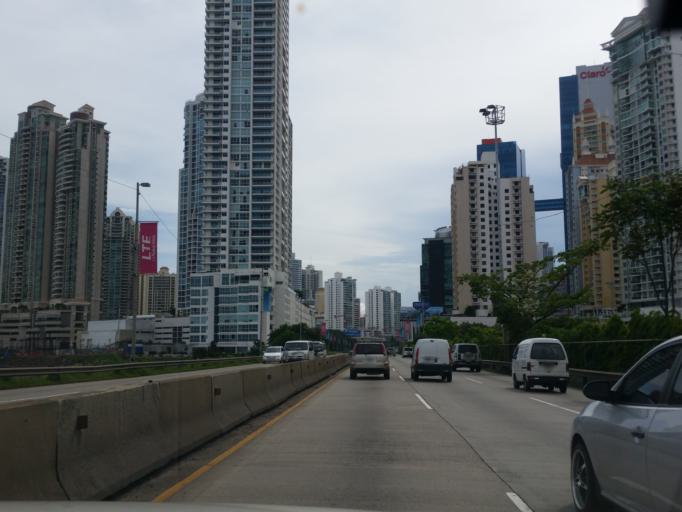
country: PA
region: Panama
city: Panama
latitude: 8.9825
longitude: -79.5051
